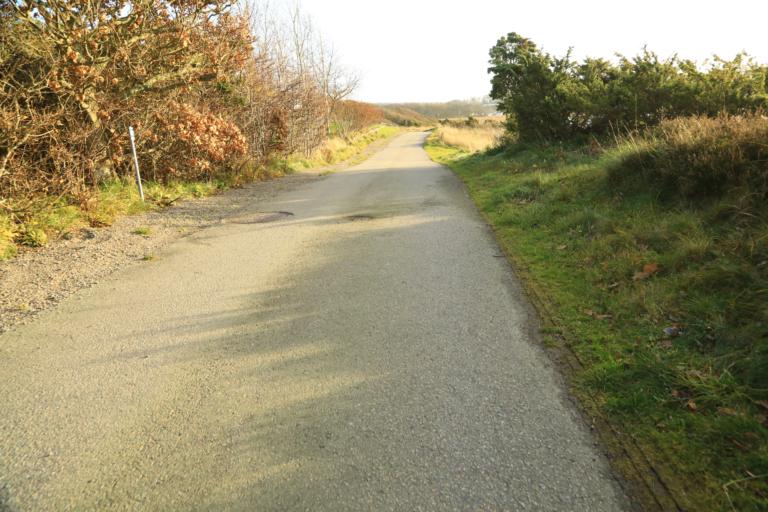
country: SE
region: Halland
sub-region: Varbergs Kommun
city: Varberg
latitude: 57.1868
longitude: 12.2104
